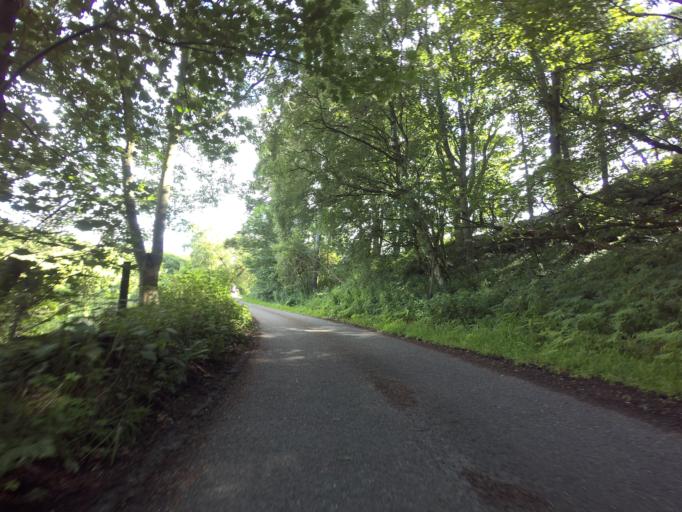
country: GB
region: Scotland
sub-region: Aberdeenshire
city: Banff
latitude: 57.6095
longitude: -2.5119
